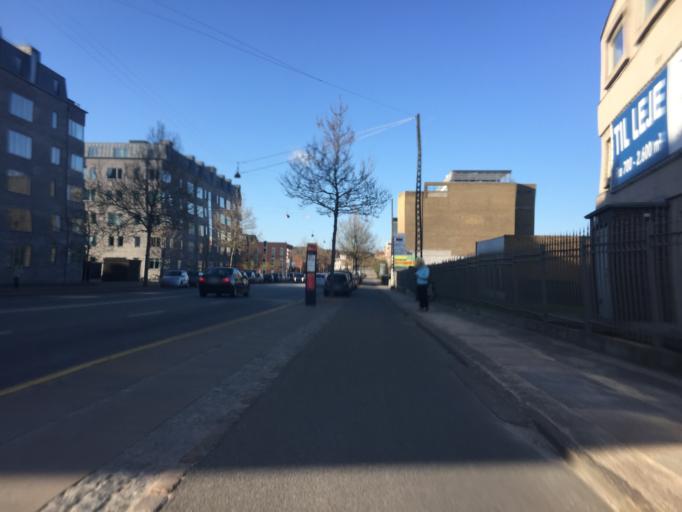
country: DK
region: Capital Region
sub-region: Frederiksberg Kommune
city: Frederiksberg
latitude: 55.6559
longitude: 12.5124
